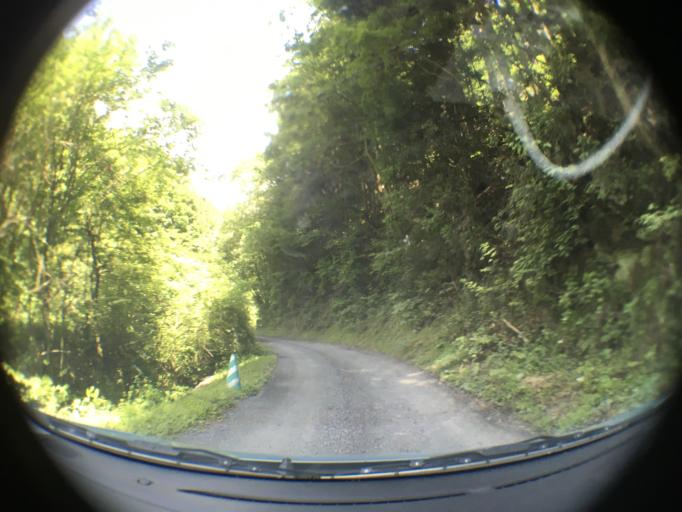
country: JP
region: Iwate
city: Ichinoseki
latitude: 38.7787
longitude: 141.4197
